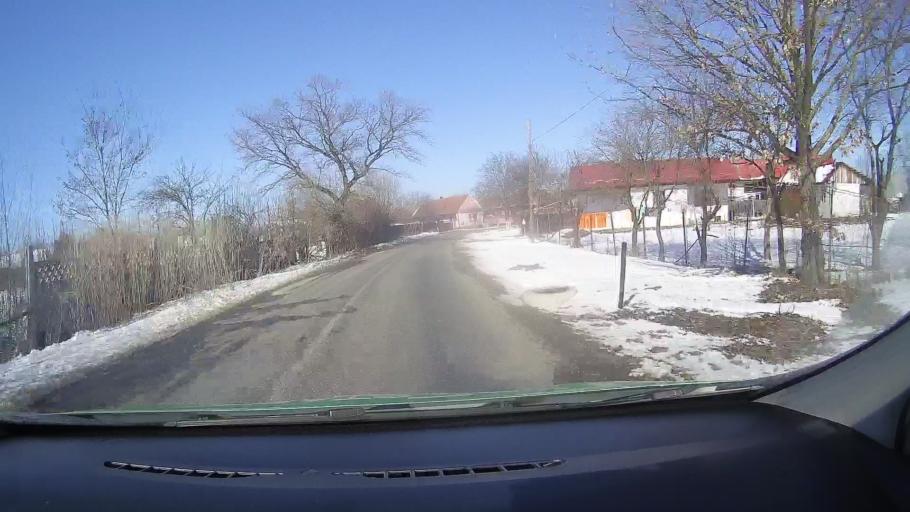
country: RO
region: Brasov
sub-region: Comuna Harseni
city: Harseni
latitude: 45.7850
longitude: 25.0000
